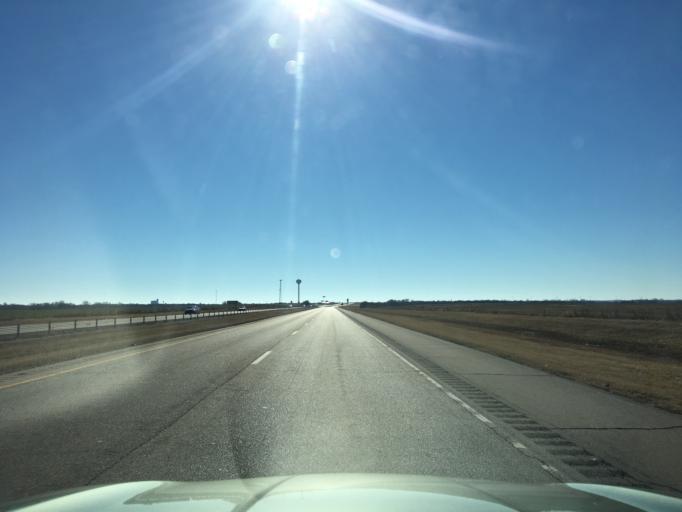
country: US
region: Oklahoma
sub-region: Kay County
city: Blackwell
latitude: 36.9543
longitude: -97.3458
